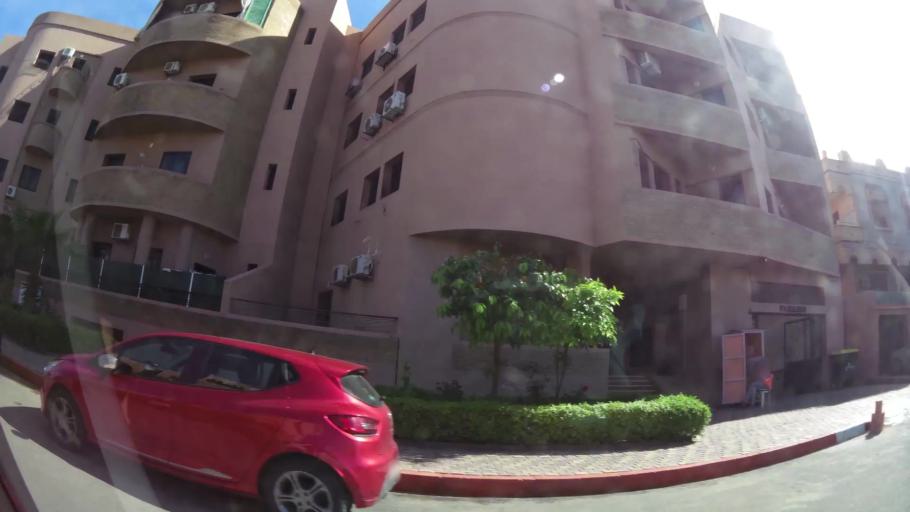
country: MA
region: Marrakech-Tensift-Al Haouz
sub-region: Marrakech
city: Marrakesh
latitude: 31.6521
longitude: -8.0135
